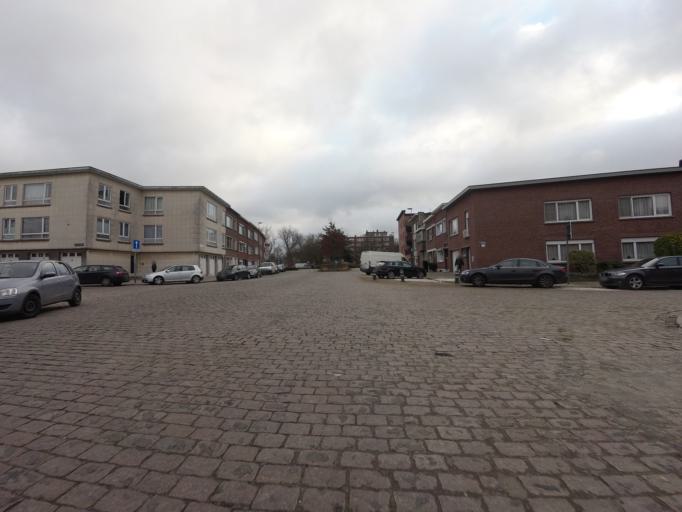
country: BE
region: Flanders
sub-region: Provincie Antwerpen
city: Hoboken
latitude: 51.1805
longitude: 4.3845
